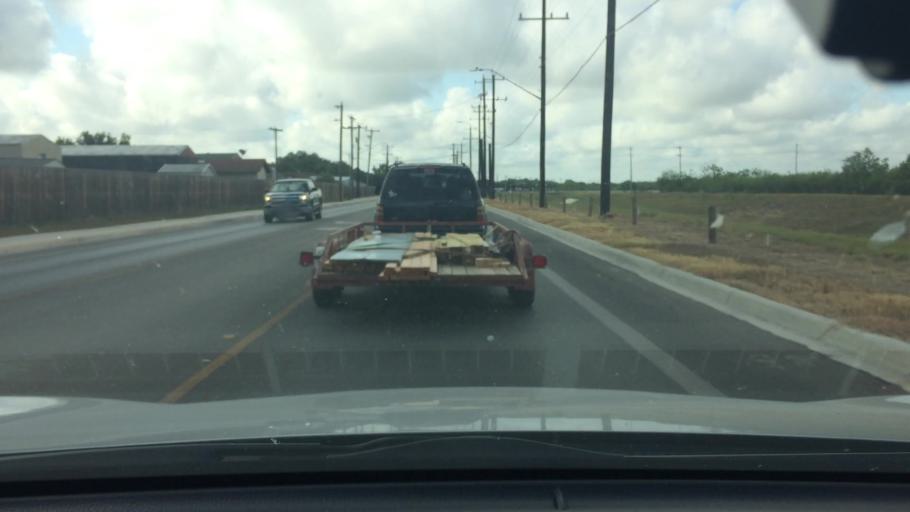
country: US
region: Texas
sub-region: Bexar County
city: China Grove
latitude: 29.3416
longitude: -98.4247
